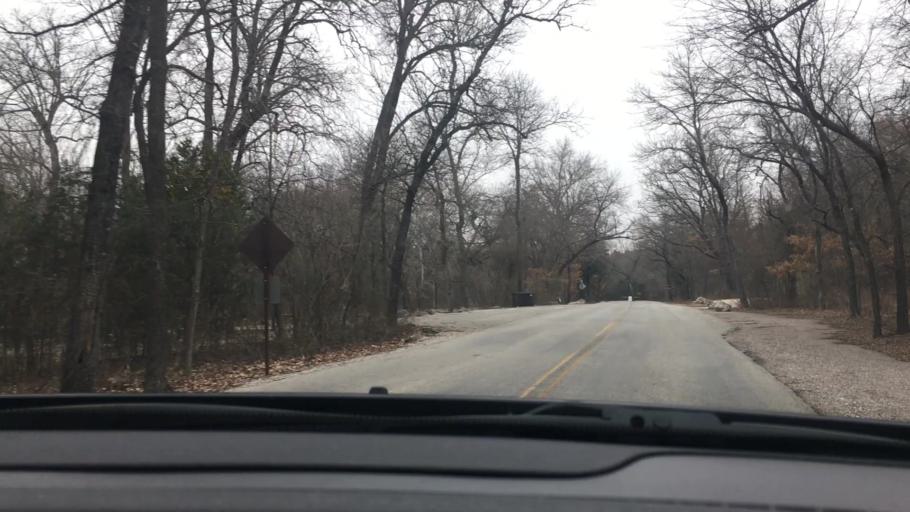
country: US
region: Oklahoma
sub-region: Murray County
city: Sulphur
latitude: 34.5018
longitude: -96.9650
